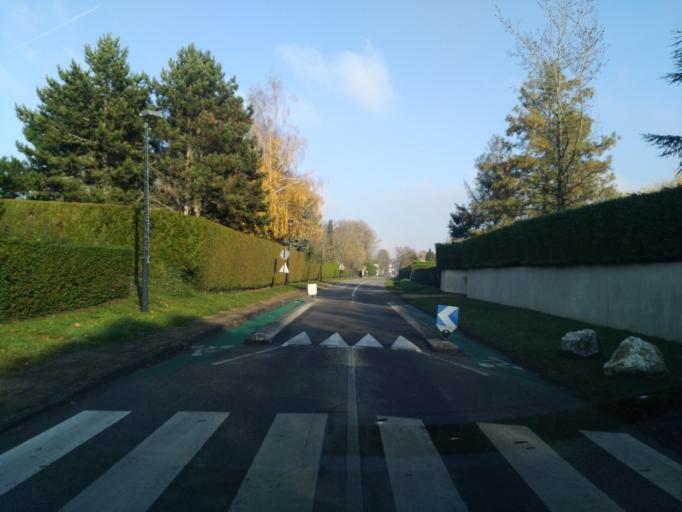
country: FR
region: Ile-de-France
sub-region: Departement des Yvelines
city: Feucherolles
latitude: 48.8804
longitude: 1.9807
